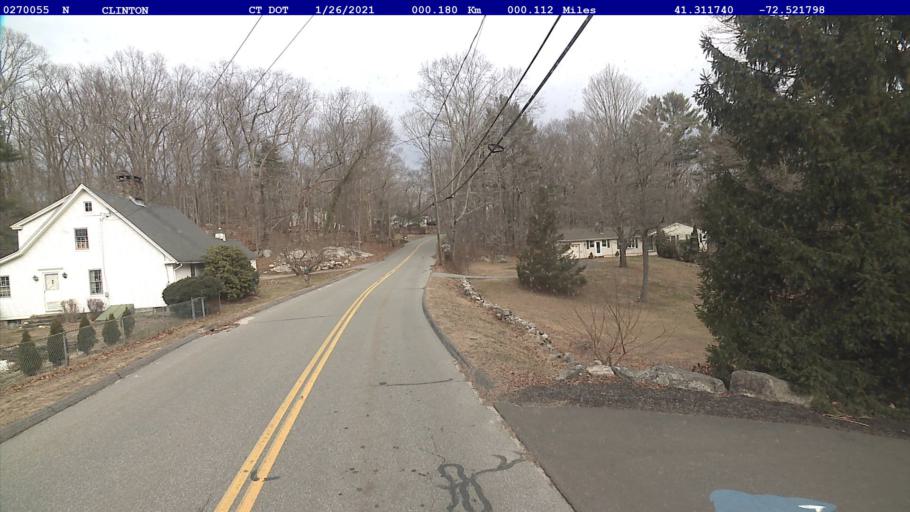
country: US
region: Connecticut
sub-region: Middlesex County
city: Clinton
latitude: 41.3117
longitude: -72.5218
